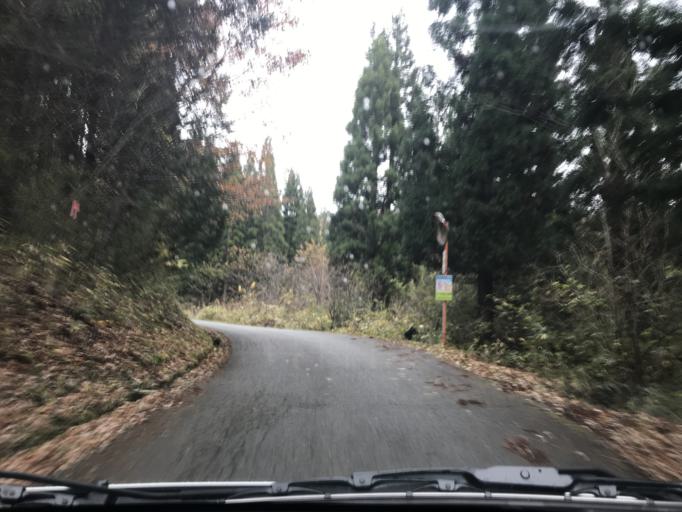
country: JP
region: Iwate
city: Ichinoseki
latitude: 38.9752
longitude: 140.9999
